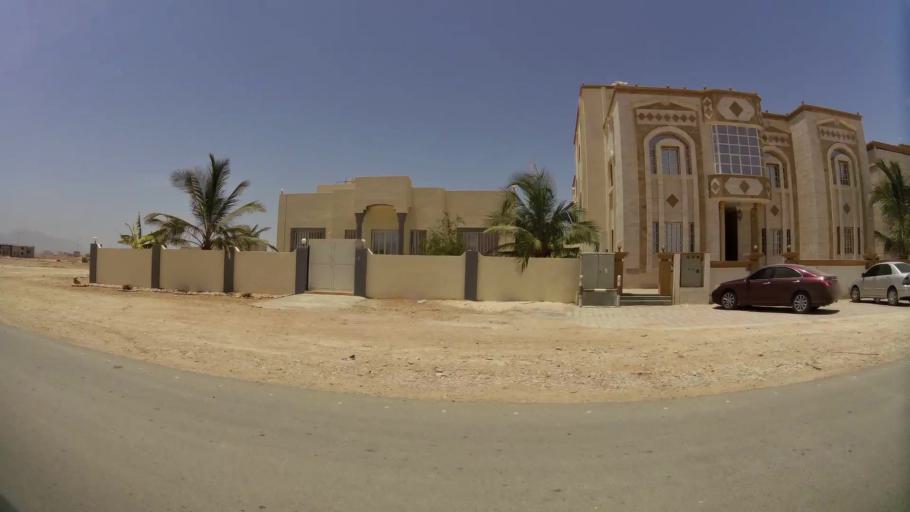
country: OM
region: Zufar
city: Salalah
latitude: 17.0963
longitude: 54.1690
